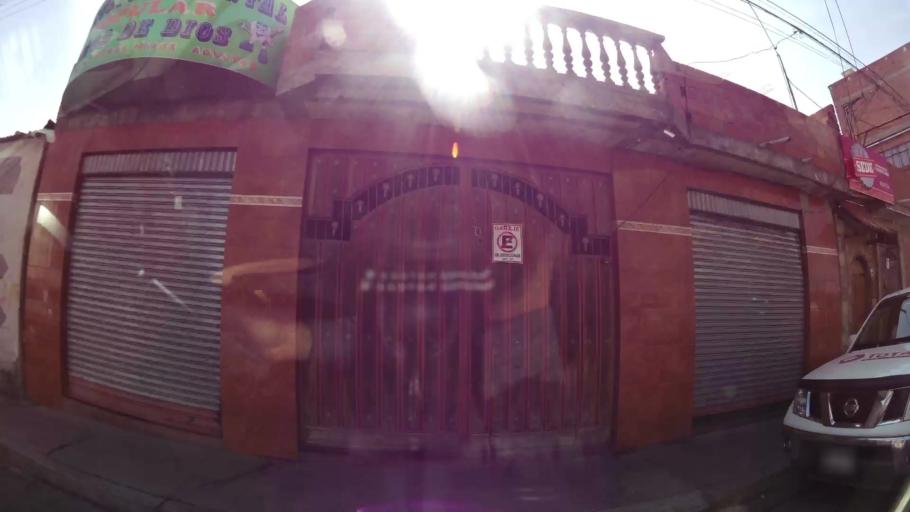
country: BO
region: La Paz
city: La Paz
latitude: -16.5080
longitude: -68.1130
